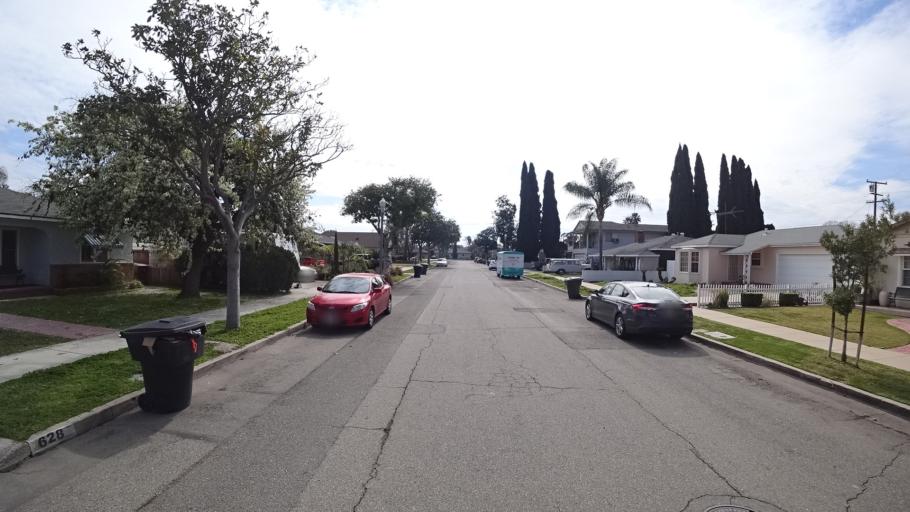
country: US
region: California
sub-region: Orange County
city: Anaheim
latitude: 33.8271
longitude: -117.9152
